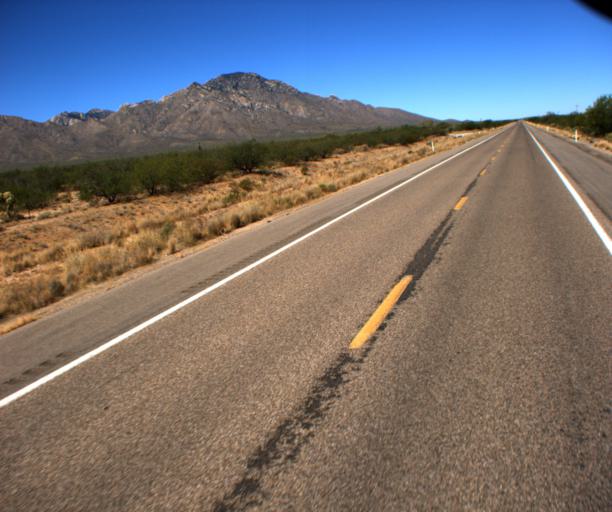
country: US
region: Arizona
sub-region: Pima County
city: Three Points
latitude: 32.0414
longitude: -111.4503
